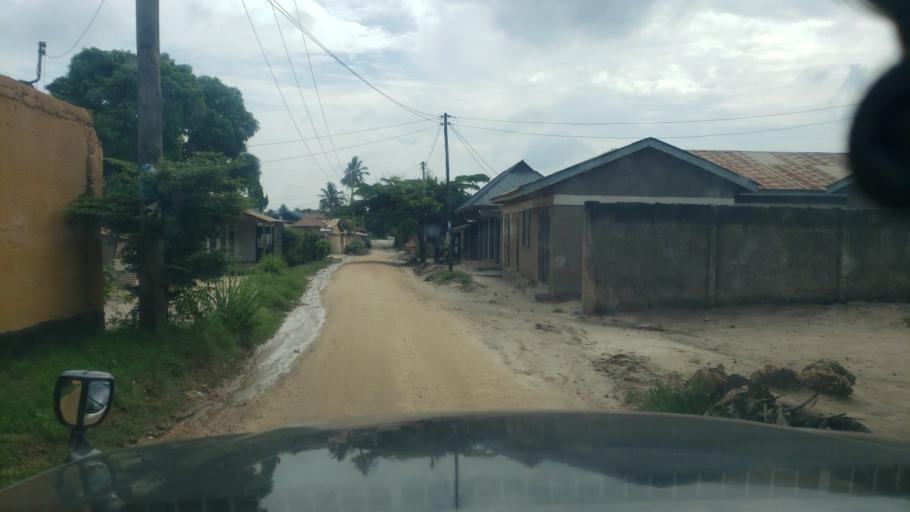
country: TZ
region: Pwani
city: Vikindu
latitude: -6.9198
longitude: 39.2553
